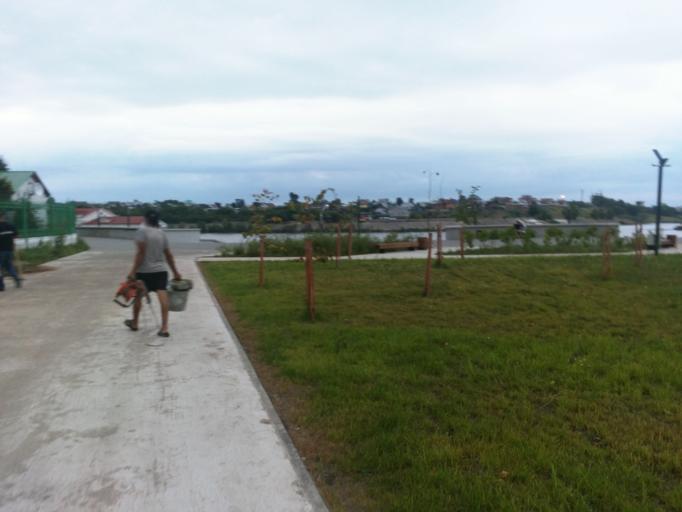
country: RU
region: Tatarstan
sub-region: Tukayevskiy Rayon
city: Naberezhnyye Chelny
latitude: 55.7020
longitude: 52.3124
